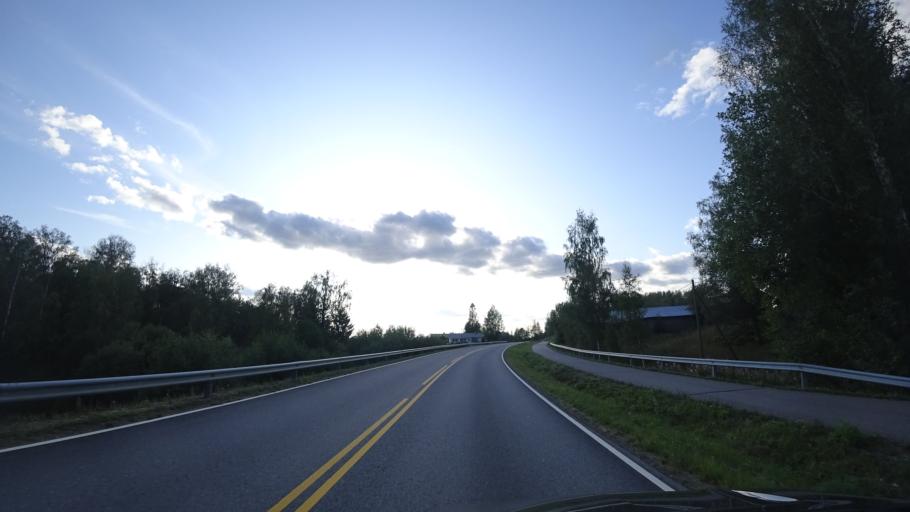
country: FI
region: Haeme
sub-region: Haemeenlinna
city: Lammi
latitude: 61.0812
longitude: 25.0586
